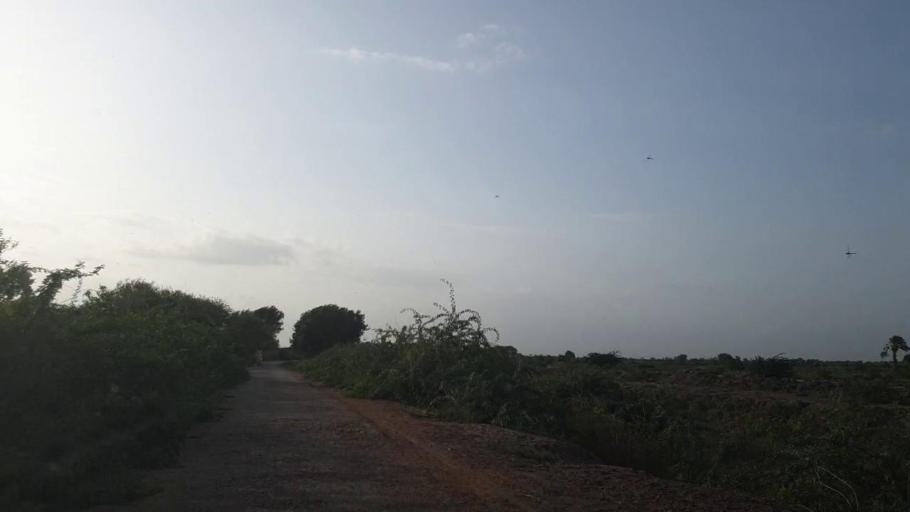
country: PK
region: Sindh
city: Kadhan
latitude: 24.6295
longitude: 69.1597
